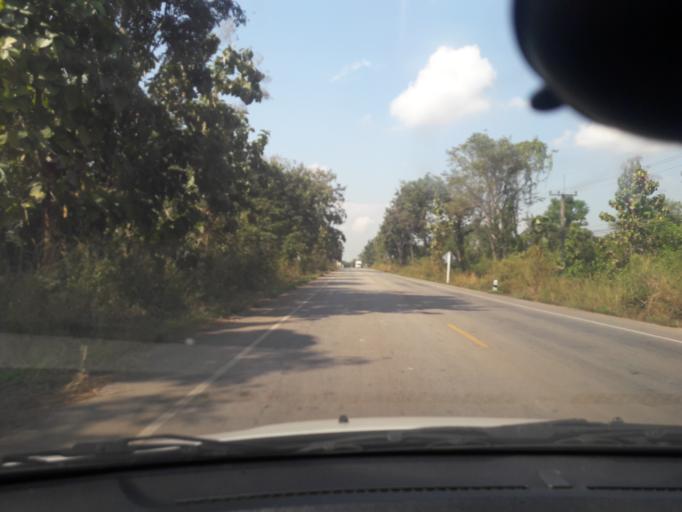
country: TH
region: Lampang
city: Mae Tha
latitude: 18.1977
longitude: 99.5123
